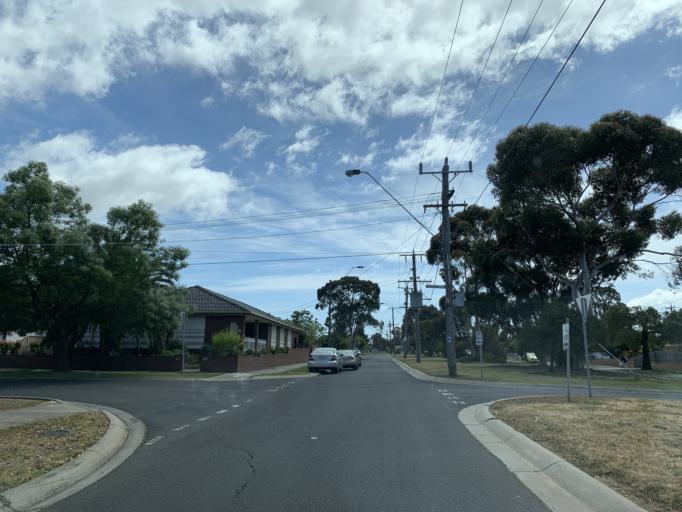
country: AU
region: Victoria
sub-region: Brimbank
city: St Albans
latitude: -37.7402
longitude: 144.8012
